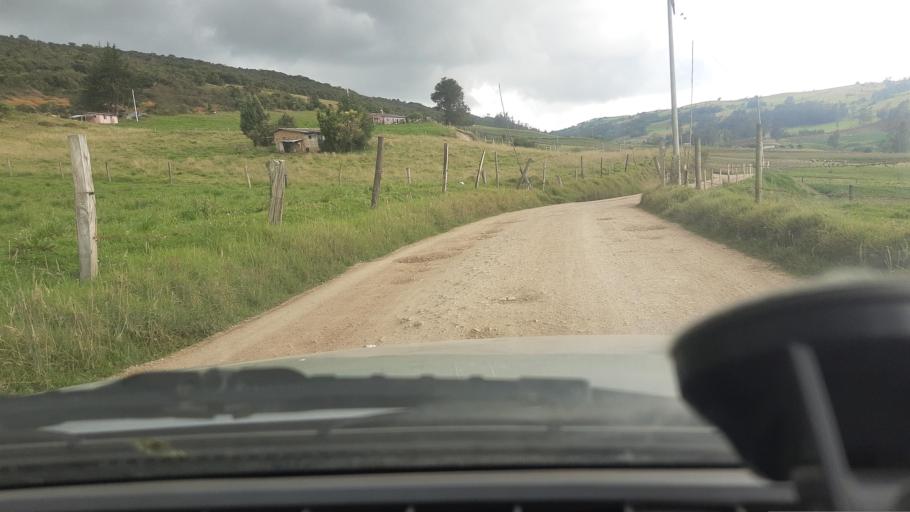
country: CO
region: Cundinamarca
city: Suesca
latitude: 5.1690
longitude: -73.7708
